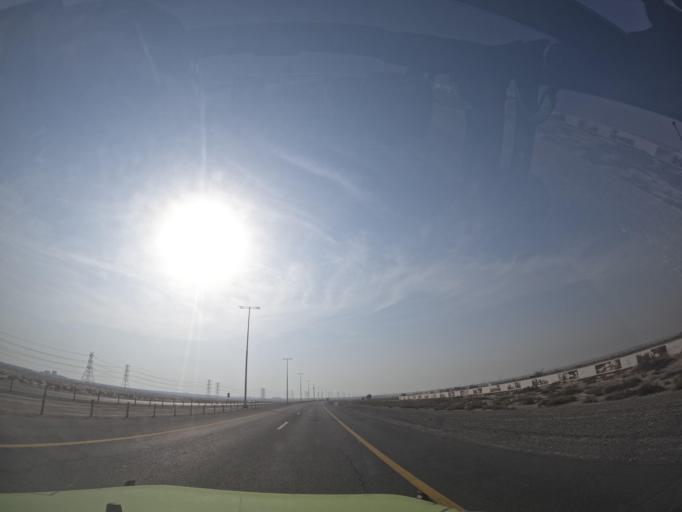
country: AE
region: Dubai
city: Dubai
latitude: 24.8399
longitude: 55.0410
